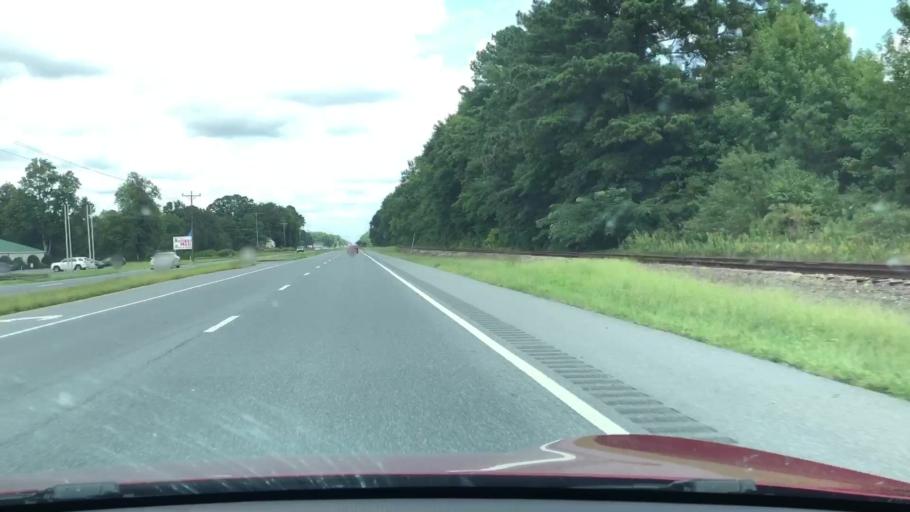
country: US
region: Virginia
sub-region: Northampton County
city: Exmore
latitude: 37.6029
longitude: -75.7736
